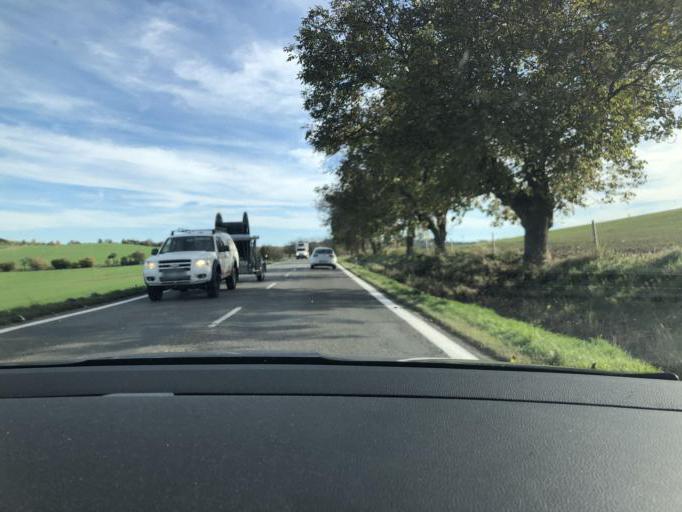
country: CZ
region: Central Bohemia
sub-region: Okres Benesov
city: Benesov
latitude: 49.7749
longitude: 14.7231
